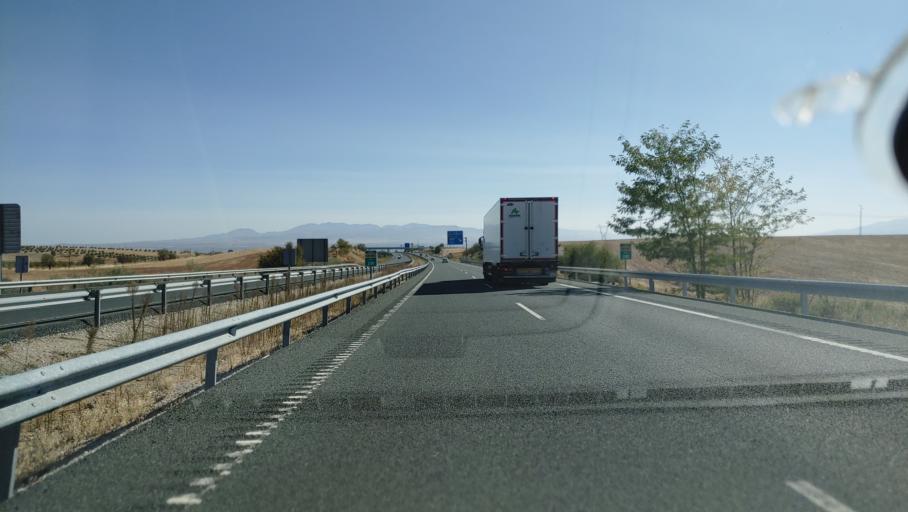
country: ES
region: Andalusia
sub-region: Provincia de Granada
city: Darro
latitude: 37.3209
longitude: -3.2806
